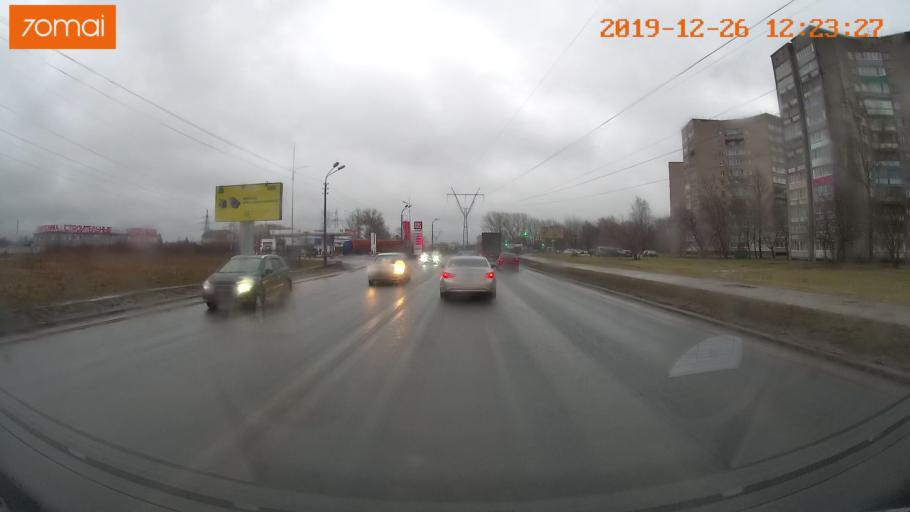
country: RU
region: Vologda
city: Tonshalovo
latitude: 59.1495
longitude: 37.9585
